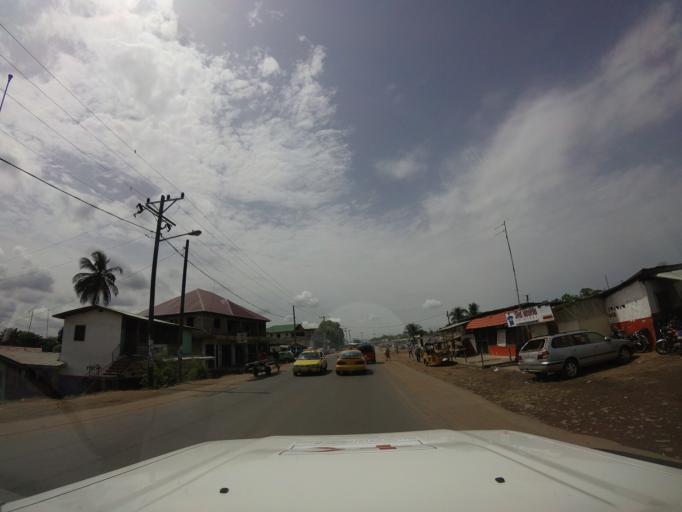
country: LR
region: Montserrado
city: Monrovia
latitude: 6.3873
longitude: -10.7815
